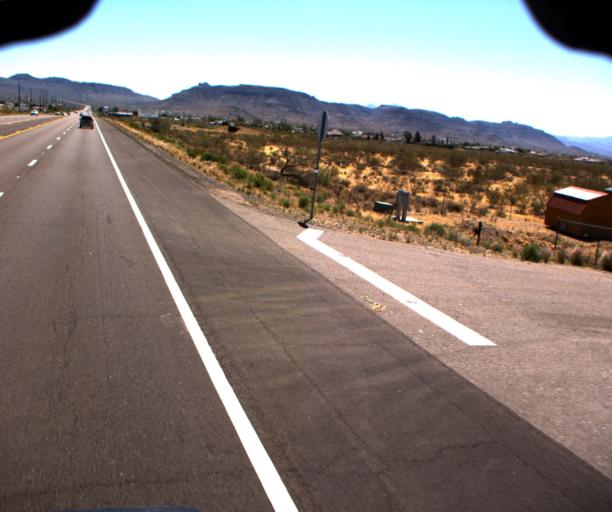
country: US
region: Arizona
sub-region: Mohave County
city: Golden Valley
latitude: 35.2206
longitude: -114.1877
